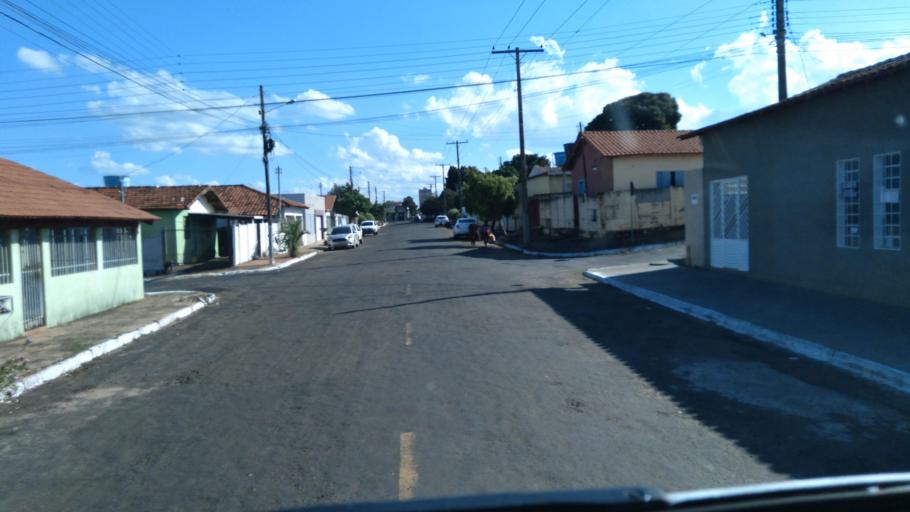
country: BR
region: Goias
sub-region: Mineiros
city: Mineiros
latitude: -17.5605
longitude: -52.5481
